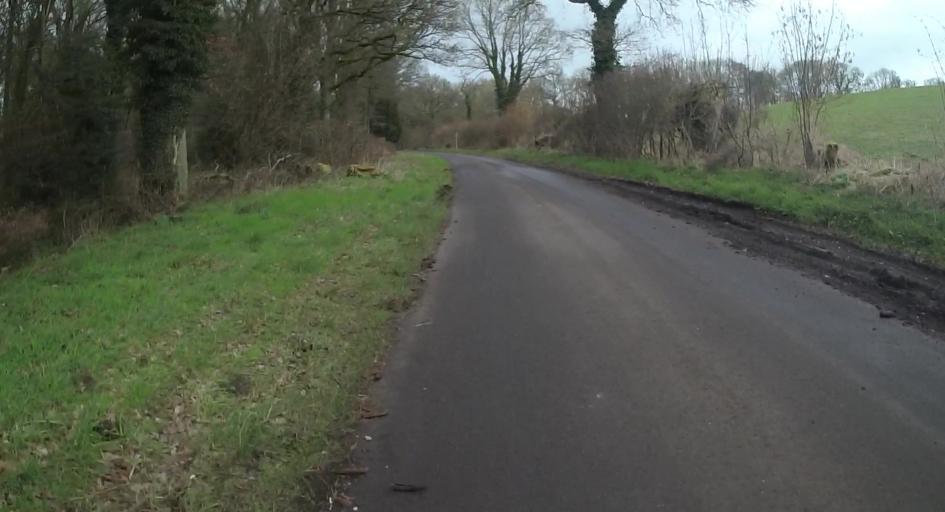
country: GB
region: England
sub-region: Hampshire
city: Kingsclere
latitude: 51.2806
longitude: -1.2024
